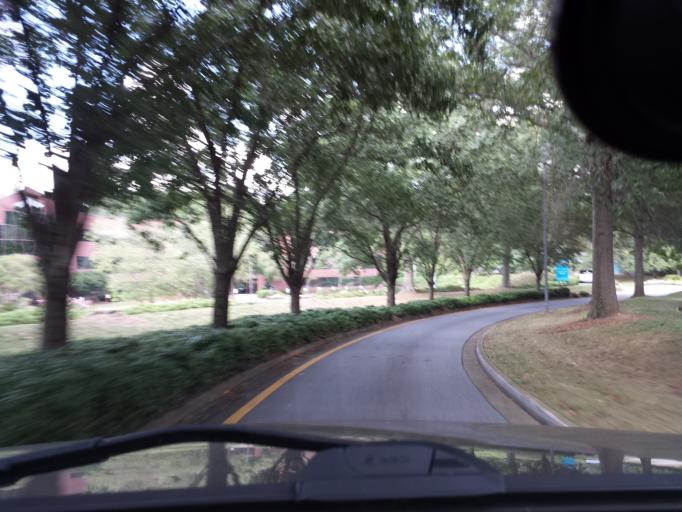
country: US
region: Georgia
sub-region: Cobb County
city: Smyrna
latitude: 33.9268
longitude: -84.4822
